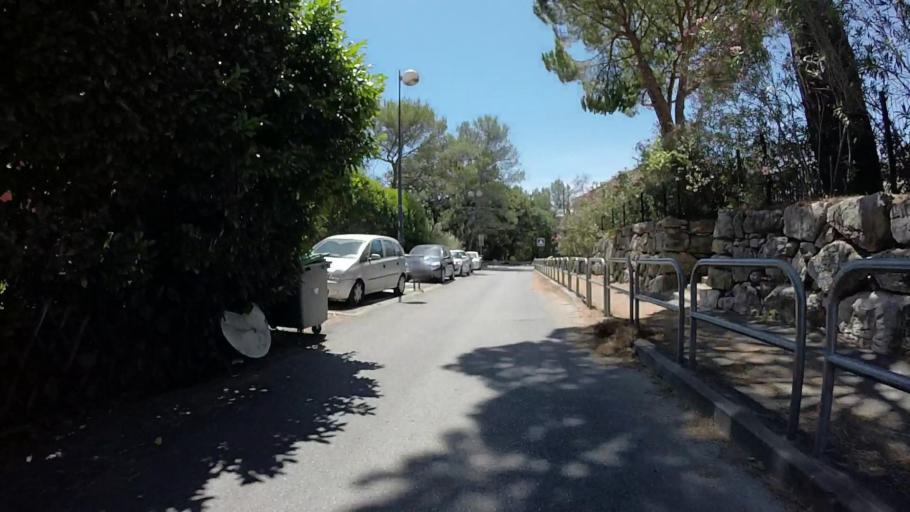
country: FR
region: Provence-Alpes-Cote d'Azur
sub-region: Departement des Alpes-Maritimes
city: Vallauris
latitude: 43.6209
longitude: 7.0442
